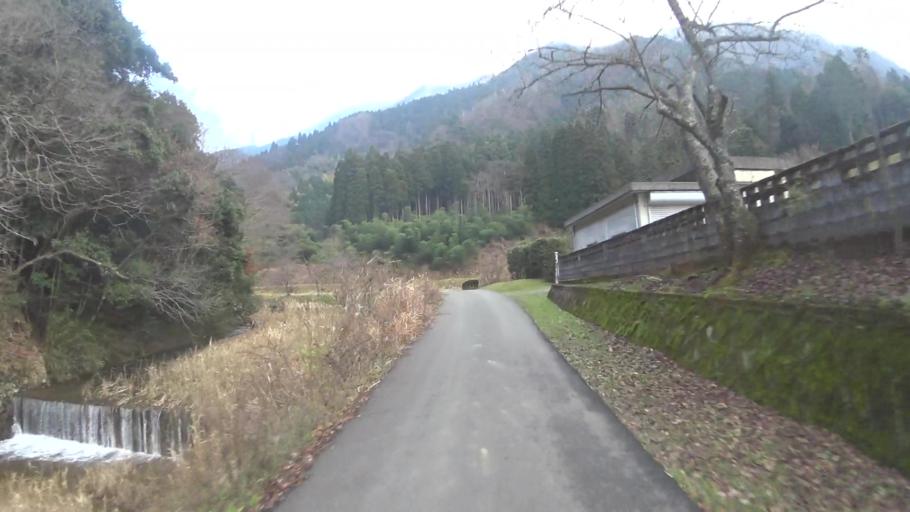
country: JP
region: Kyoto
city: Maizuru
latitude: 35.4442
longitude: 135.4370
